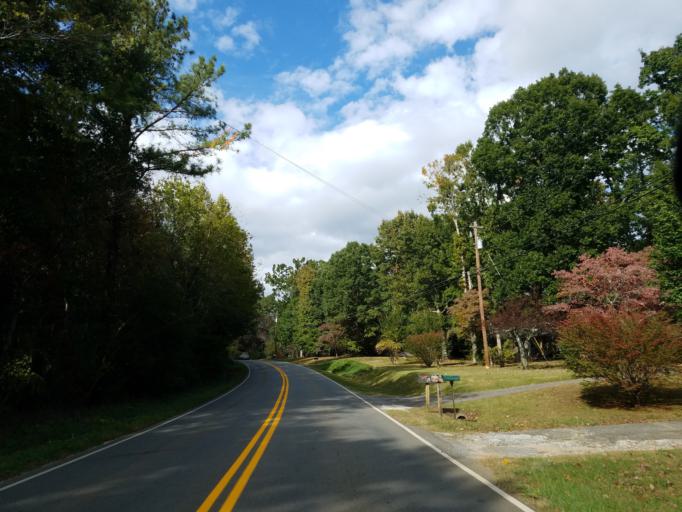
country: US
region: Georgia
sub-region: Pickens County
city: Jasper
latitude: 34.4319
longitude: -84.4211
